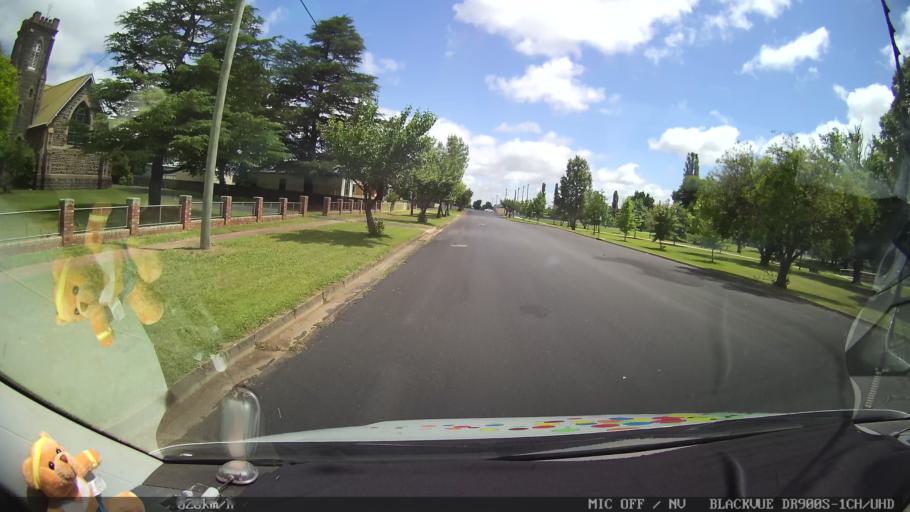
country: AU
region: New South Wales
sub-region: Glen Innes Severn
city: Glen Innes
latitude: -29.7360
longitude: 151.7328
